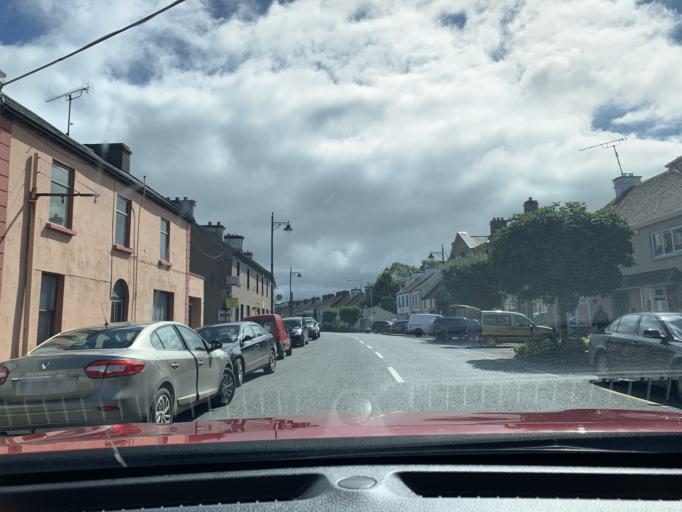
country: IE
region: Connaught
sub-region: County Leitrim
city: Carrick-on-Shannon
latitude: 53.8459
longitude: -8.1953
